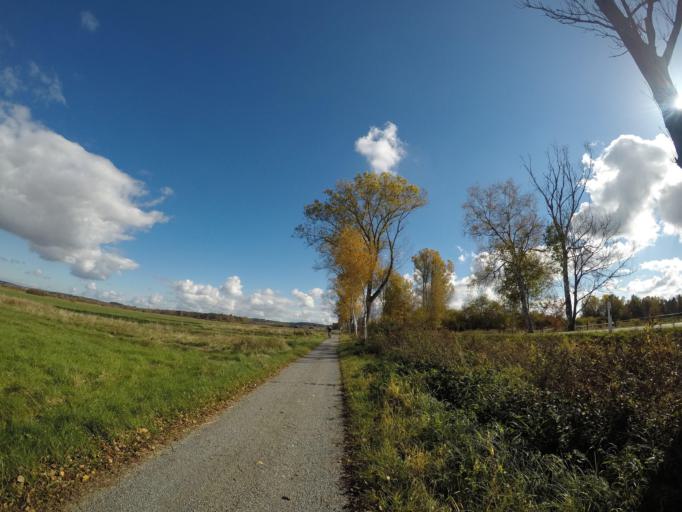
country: DE
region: Baden-Wuerttemberg
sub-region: Tuebingen Region
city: Bad Buchau
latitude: 48.0661
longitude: 9.6196
